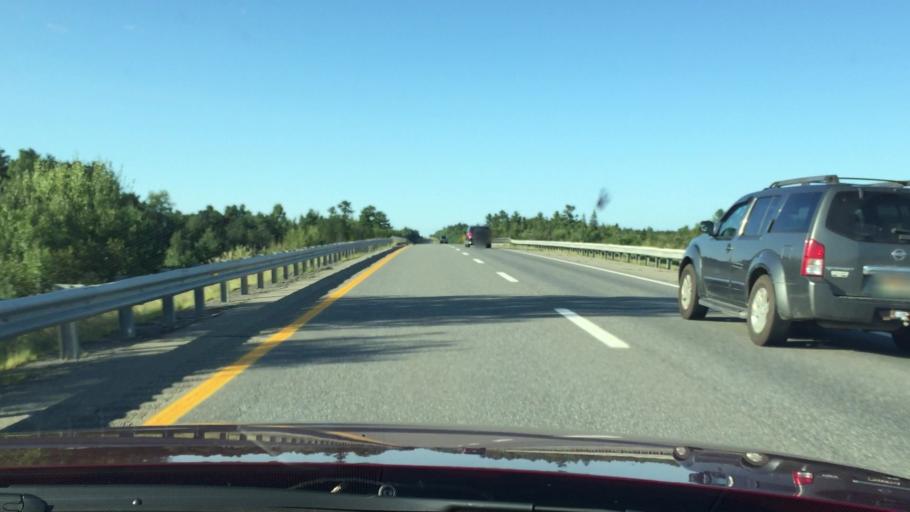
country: US
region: Maine
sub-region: Penobscot County
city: Lincoln
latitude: 45.3943
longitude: -68.6009
